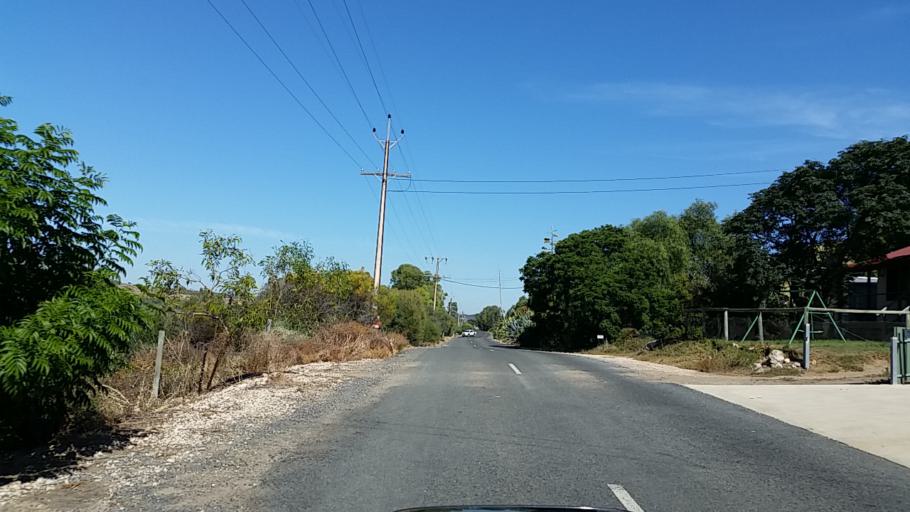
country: AU
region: South Australia
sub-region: Mid Murray
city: Mannum
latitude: -34.7043
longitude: 139.5700
